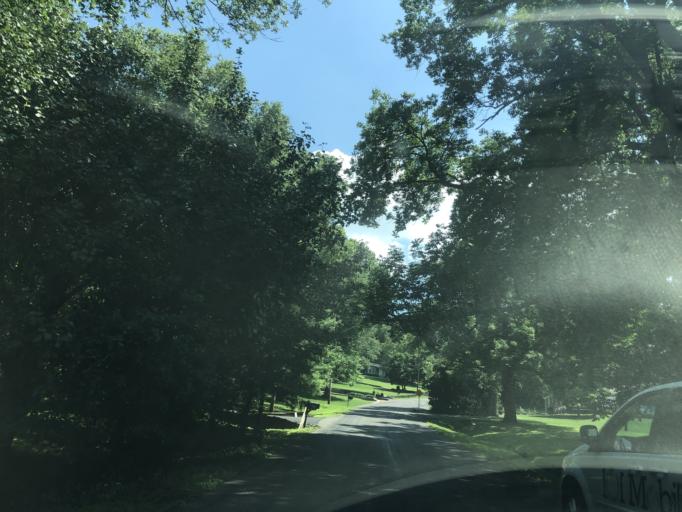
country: US
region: Tennessee
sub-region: Davidson County
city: Lakewood
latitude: 36.1795
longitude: -86.6694
